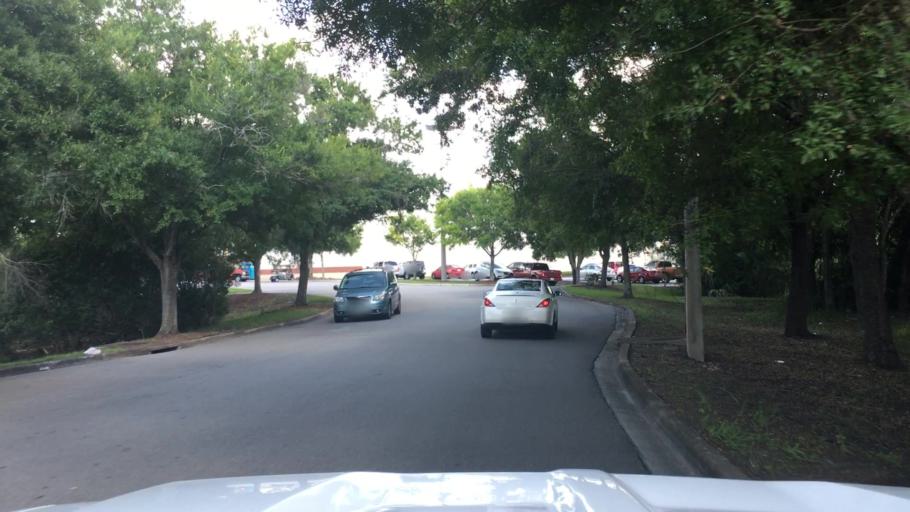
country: US
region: Florida
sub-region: Hillsborough County
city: Sun City Center
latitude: 27.7114
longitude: -82.3556
